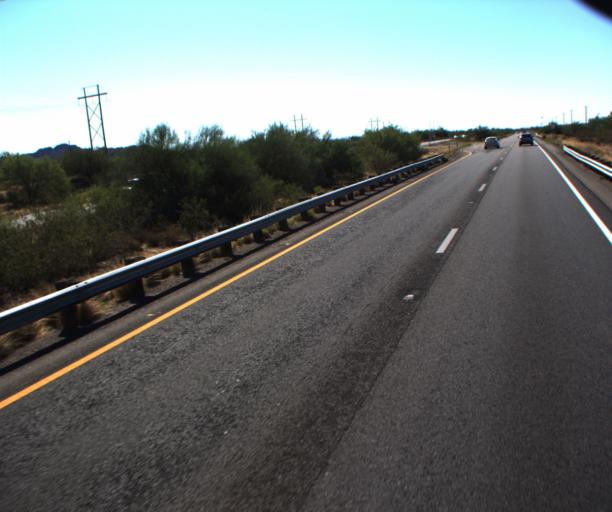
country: US
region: Arizona
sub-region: Pinal County
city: Apache Junction
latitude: 33.3745
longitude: -111.4859
